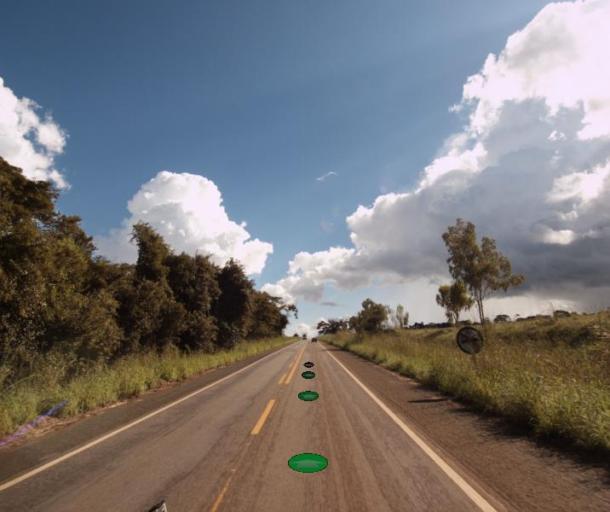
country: BR
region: Goias
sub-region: Itaberai
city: Itaberai
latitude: -15.9802
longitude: -49.6868
